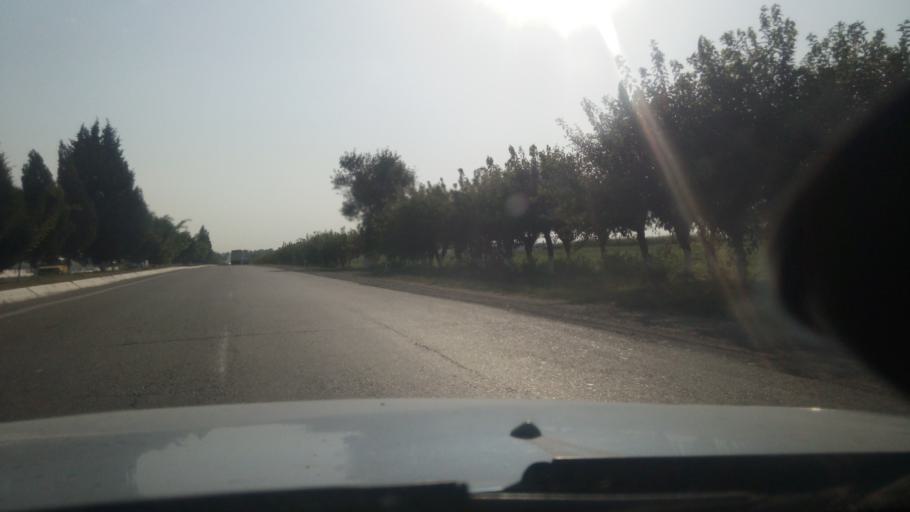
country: UZ
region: Toshkent
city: Zafar
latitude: 41.0265
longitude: 68.8612
